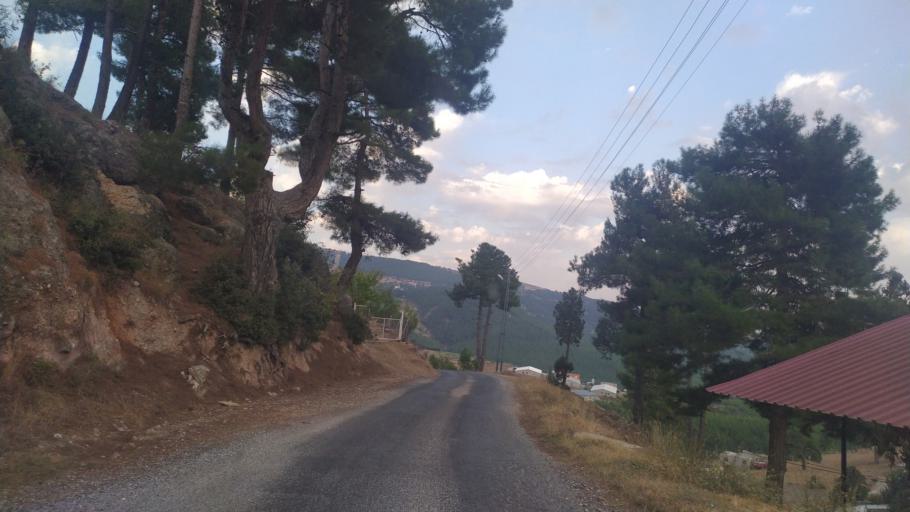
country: TR
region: Mersin
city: Camliyayla
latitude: 37.2310
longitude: 34.7135
